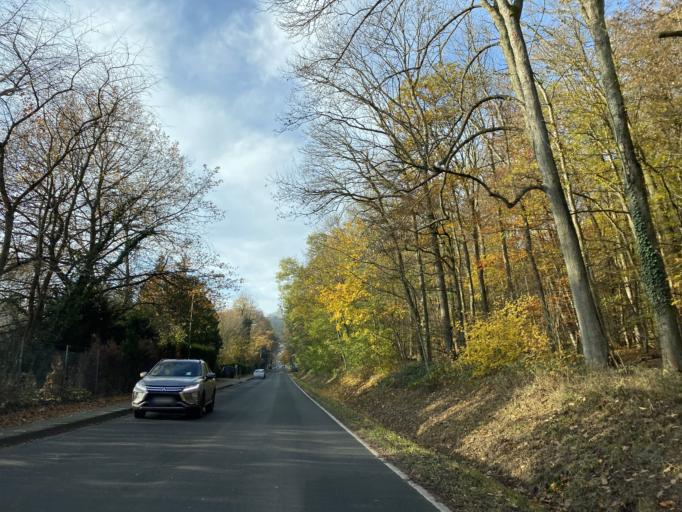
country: DE
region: Hesse
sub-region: Regierungsbezirk Darmstadt
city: Konigstein im Taunus
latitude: 50.1883
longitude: 8.4892
